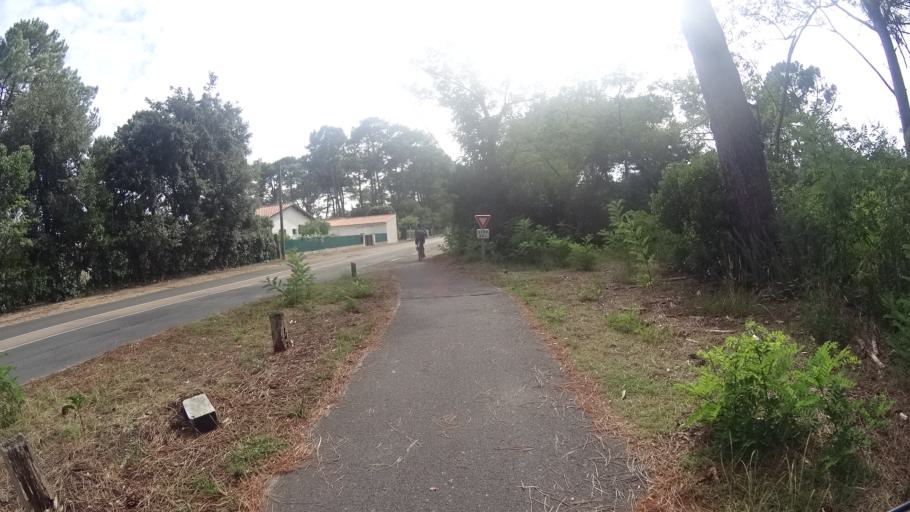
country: FR
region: Aquitaine
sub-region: Departement de la Gironde
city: Lacanau
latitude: 44.9965
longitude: -1.1425
